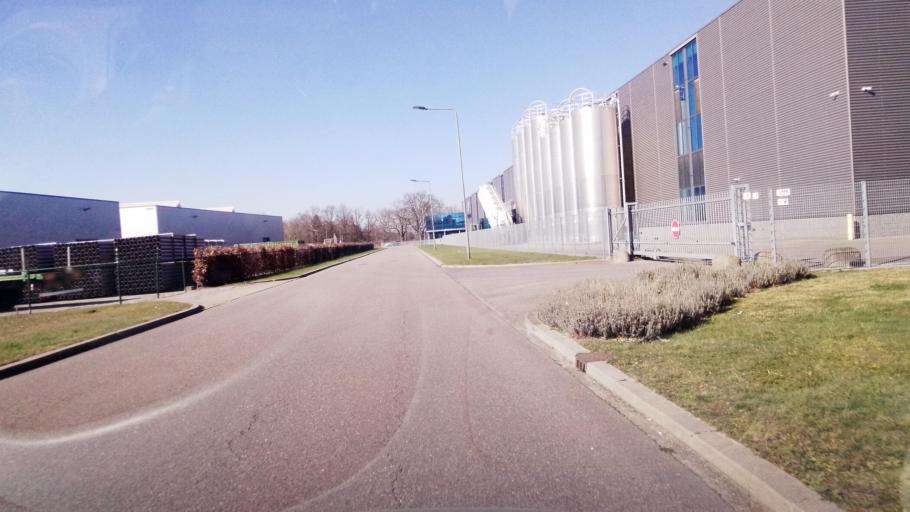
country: NL
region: Limburg
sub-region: Gemeente Peel en Maas
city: Maasbree
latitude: 51.4481
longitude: 6.0772
